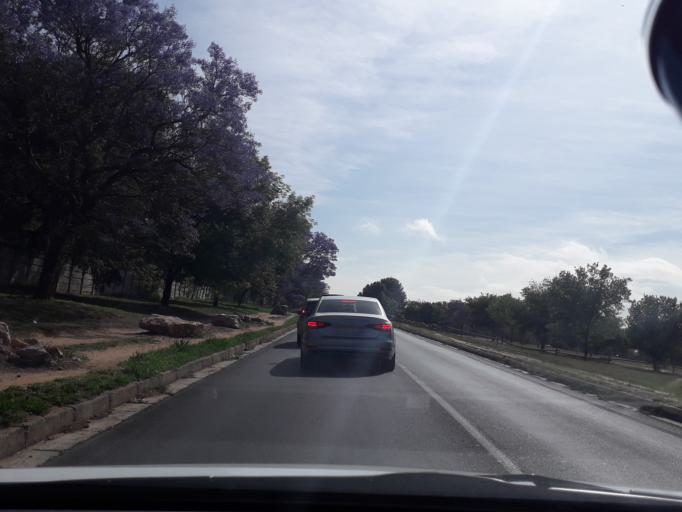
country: ZA
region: Gauteng
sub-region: City of Johannesburg Metropolitan Municipality
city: Roodepoort
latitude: -26.1127
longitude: 27.9478
